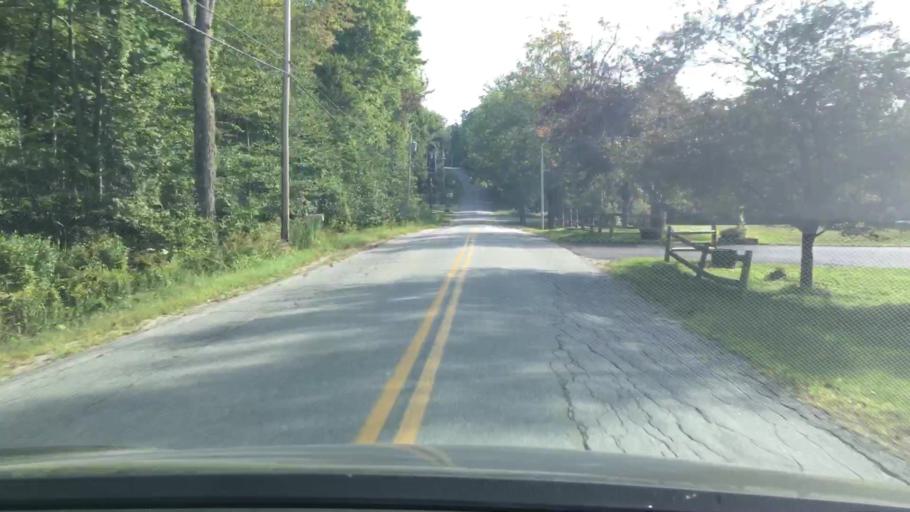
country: US
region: Maine
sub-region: Hancock County
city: Bucksport
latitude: 44.5533
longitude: -68.7957
